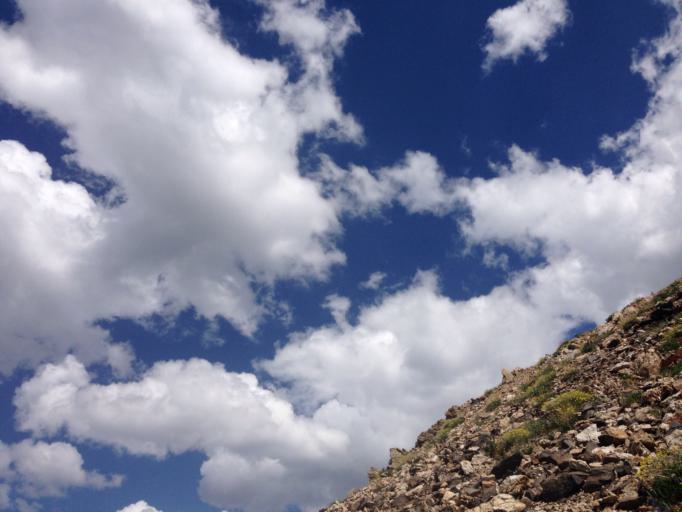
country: US
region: Colorado
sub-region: Larimer County
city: Estes Park
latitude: 40.4937
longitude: -105.8906
